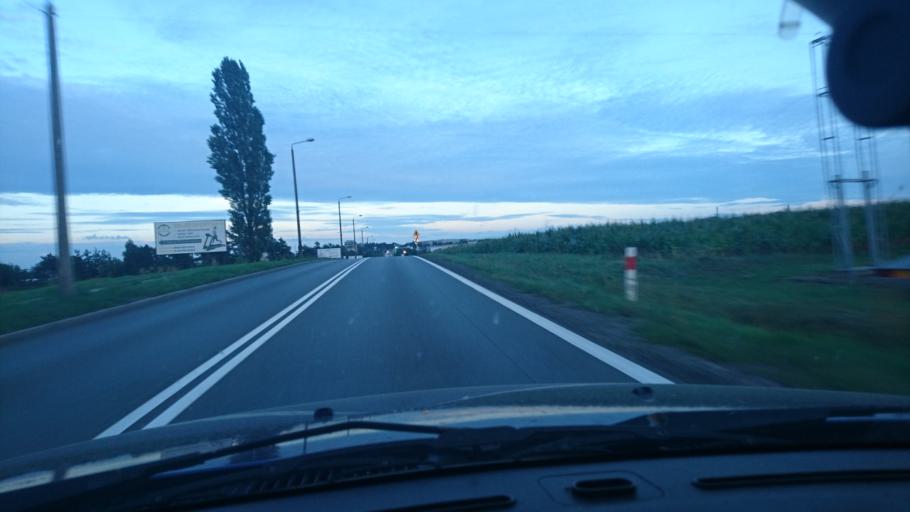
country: PL
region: Silesian Voivodeship
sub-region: Powiat tarnogorski
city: Tarnowskie Gory
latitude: 50.4611
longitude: 18.8240
